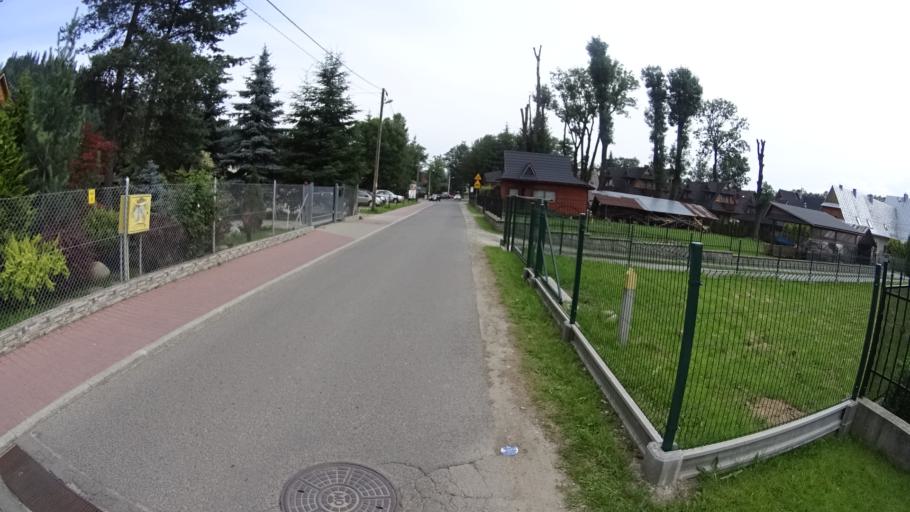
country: PL
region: Lesser Poland Voivodeship
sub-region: Powiat tatrzanski
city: Poronin
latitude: 49.3193
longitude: 19.9799
